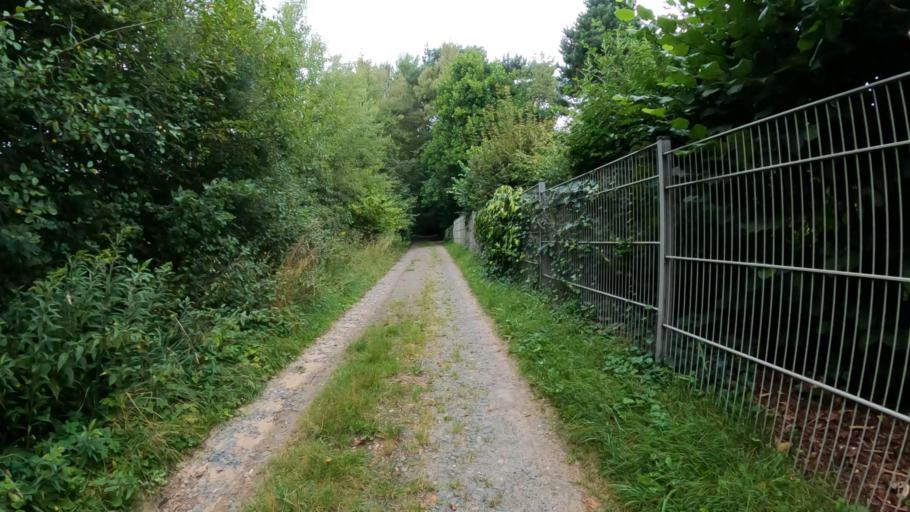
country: DE
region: Lower Saxony
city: Kakenstorf
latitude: 53.3106
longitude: 9.7856
